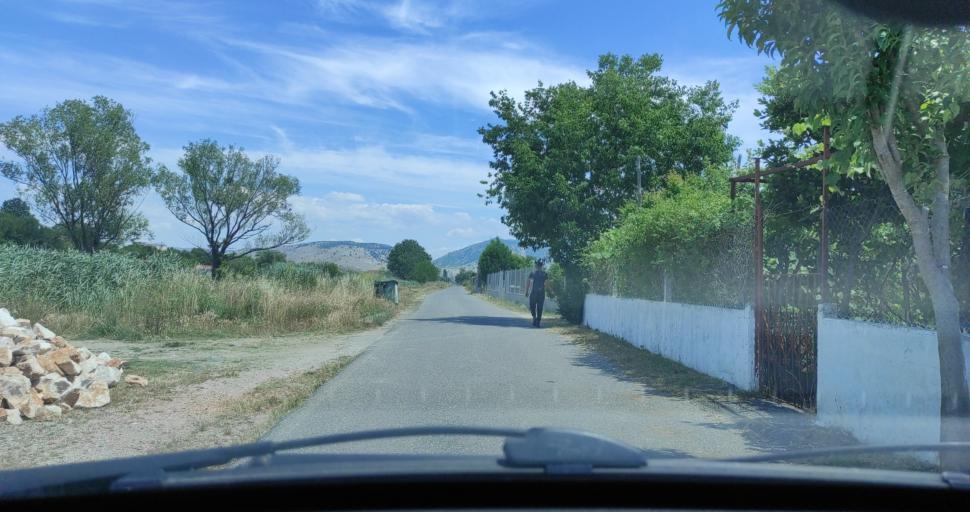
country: AL
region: Shkoder
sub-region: Rrethi i Shkodres
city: Velipoje
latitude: 41.8786
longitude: 19.3865
